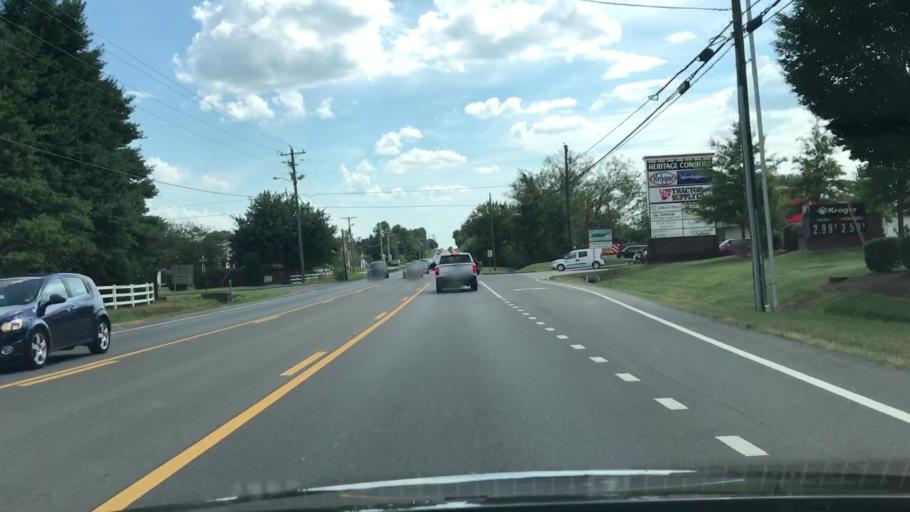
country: US
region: Tennessee
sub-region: Williamson County
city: Thompson's Station
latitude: 35.7844
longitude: -86.9127
